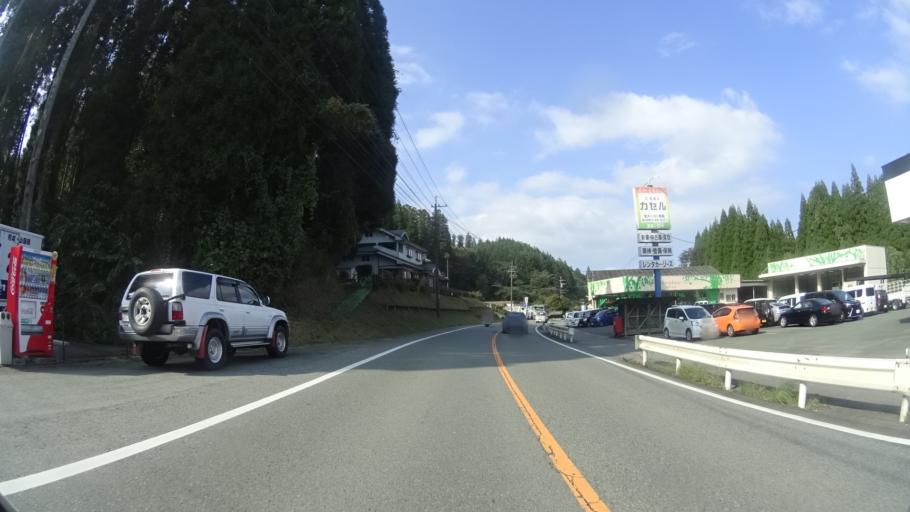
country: JP
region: Kumamoto
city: Aso
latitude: 33.1165
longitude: 131.0586
